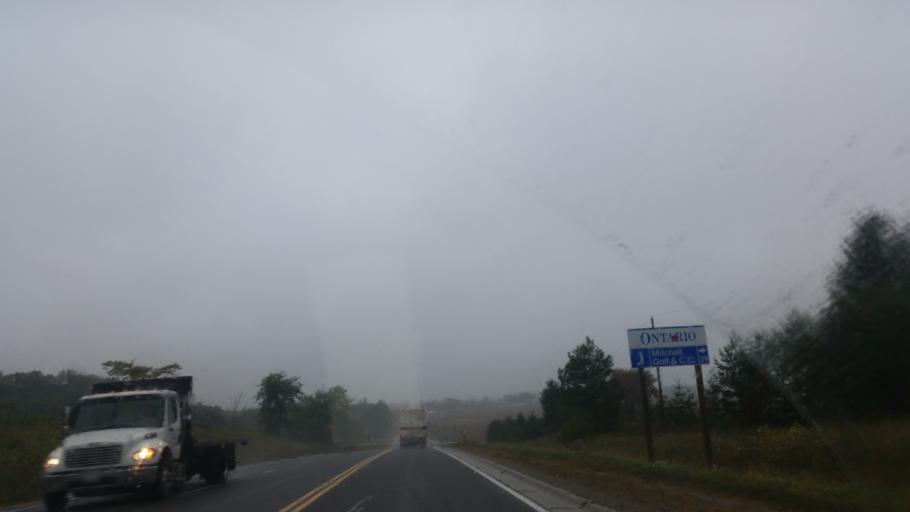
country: CA
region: Ontario
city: London
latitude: 43.1711
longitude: -81.3395
